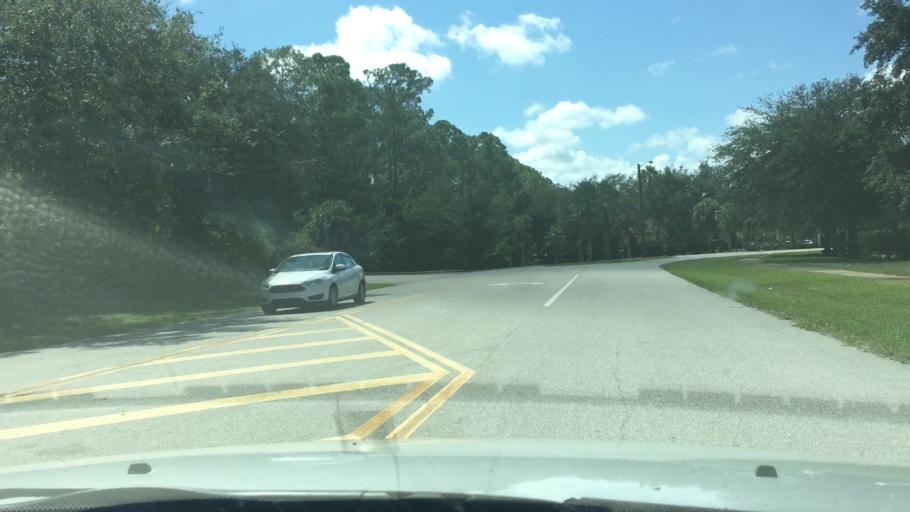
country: US
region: Florida
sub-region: Volusia County
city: Daytona Beach
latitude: 29.2036
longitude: -81.0739
